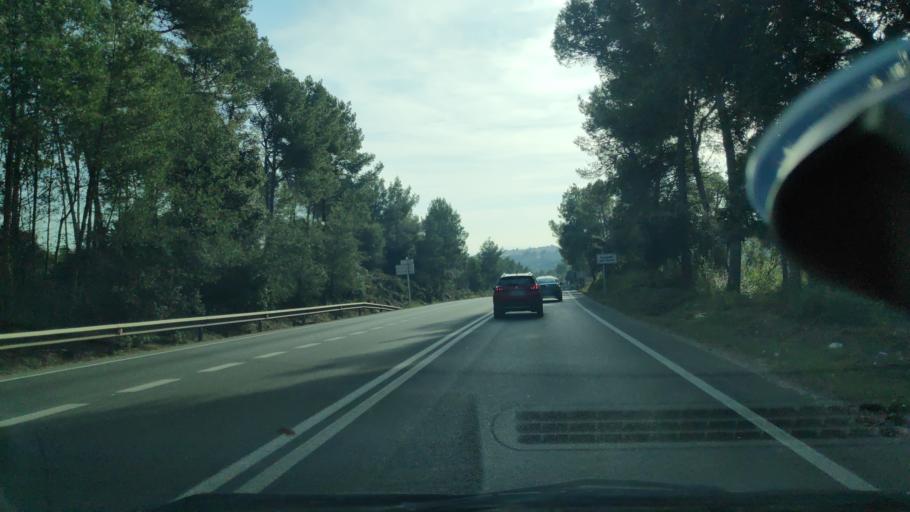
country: ES
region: Catalonia
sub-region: Provincia de Barcelona
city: Castellar del Valles
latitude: 41.5847
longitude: 2.0904
